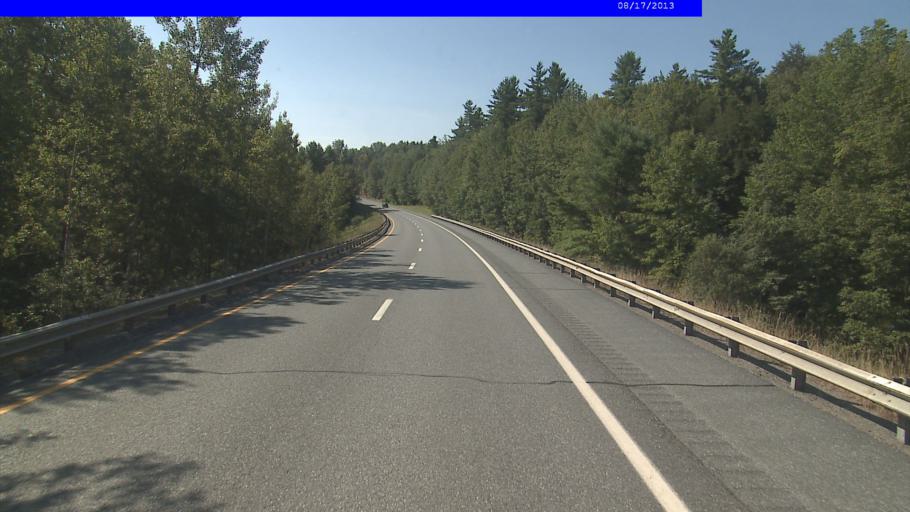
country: US
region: Vermont
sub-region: Windsor County
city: Springfield
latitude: 43.3341
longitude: -72.4217
